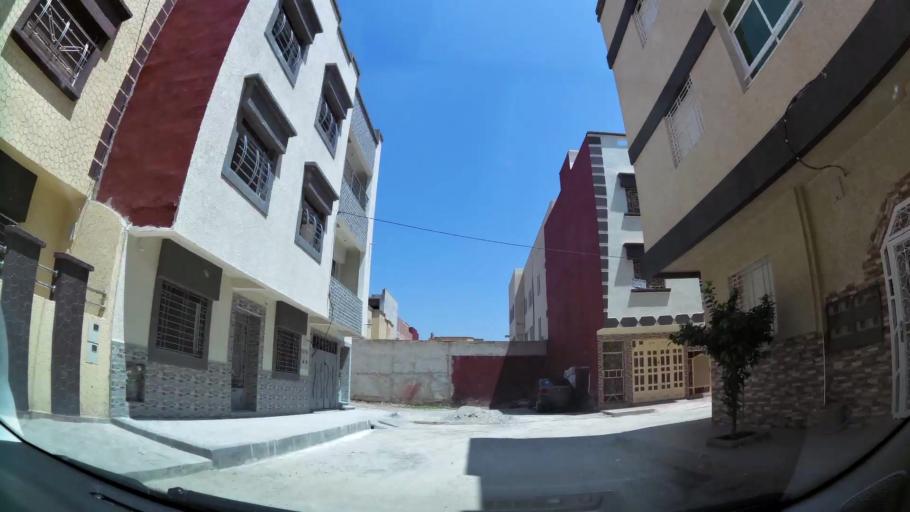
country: MA
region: Oriental
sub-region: Oujda-Angad
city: Oujda
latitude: 34.6959
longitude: -1.8847
